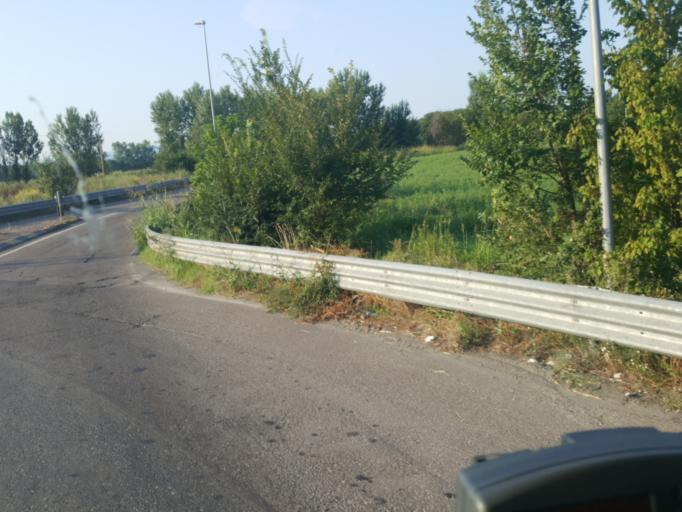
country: IT
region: Emilia-Romagna
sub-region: Provincia di Modena
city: San Vito
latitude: 44.5335
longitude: 10.9849
